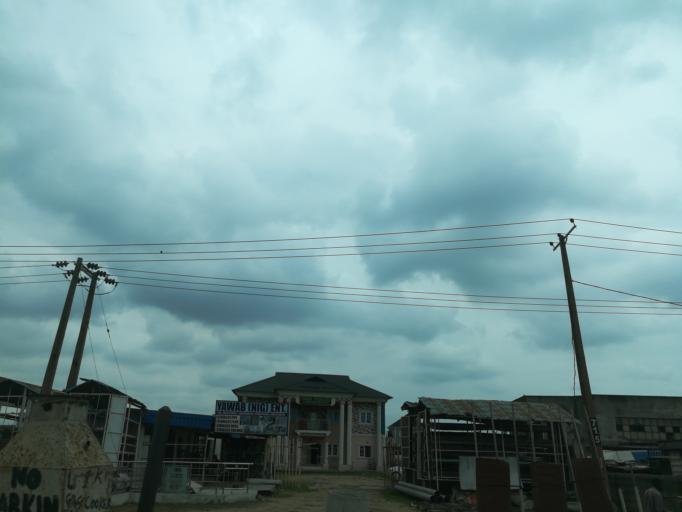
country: NG
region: Lagos
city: Ojota
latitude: 6.6094
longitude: 3.4097
